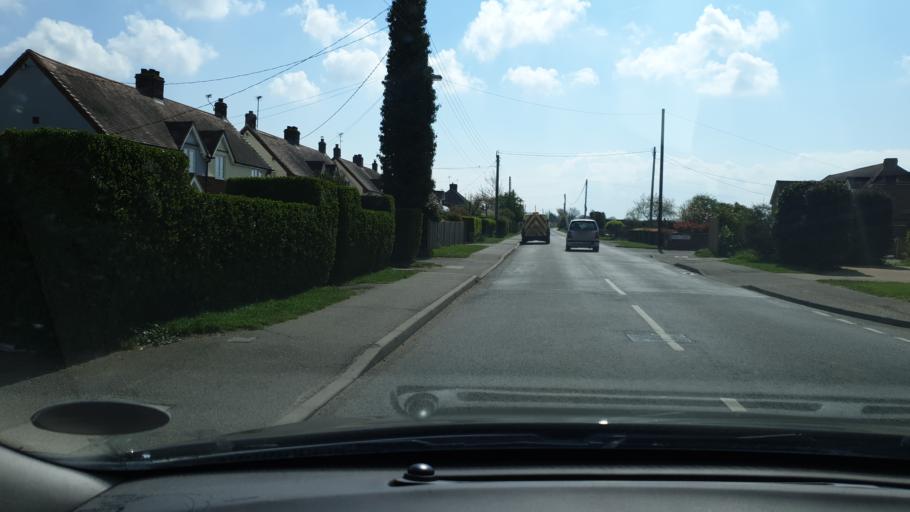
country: GB
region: England
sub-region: Essex
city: Great Bentley
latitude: 51.8508
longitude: 1.0653
